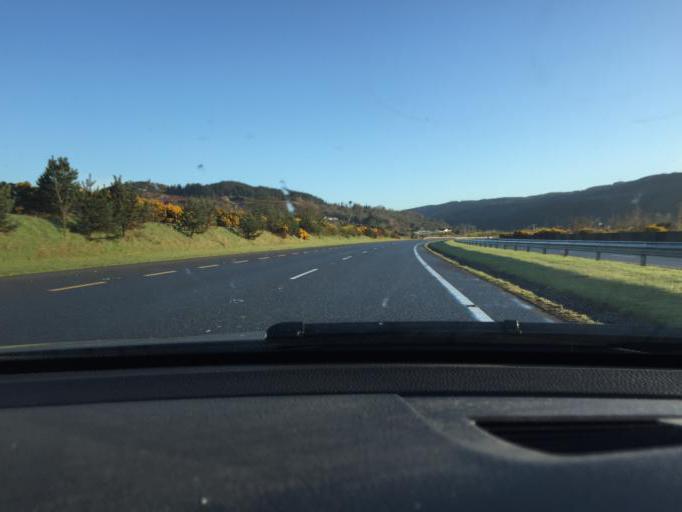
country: IE
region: Leinster
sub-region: Lu
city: Dundalk
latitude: 54.0569
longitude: -6.3580
